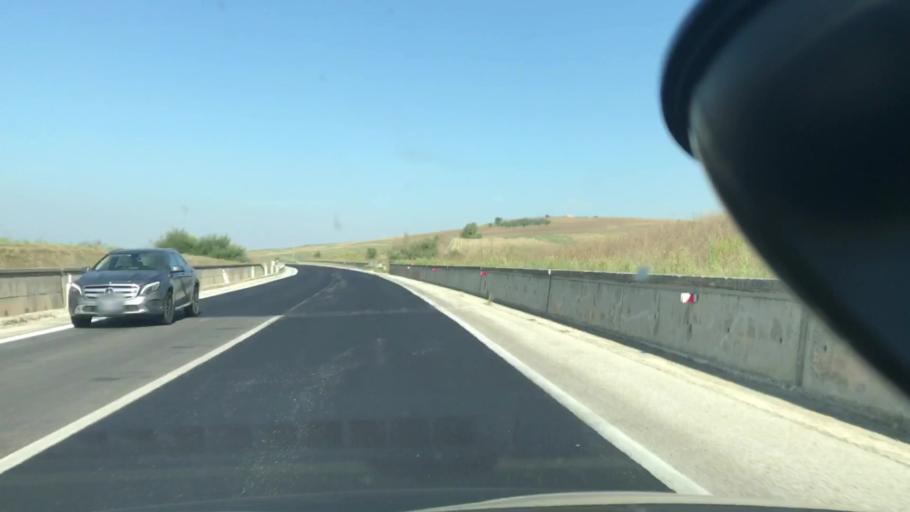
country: IT
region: Apulia
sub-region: Provincia di Barletta - Andria - Trani
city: Spinazzola
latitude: 40.9199
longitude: 16.0982
